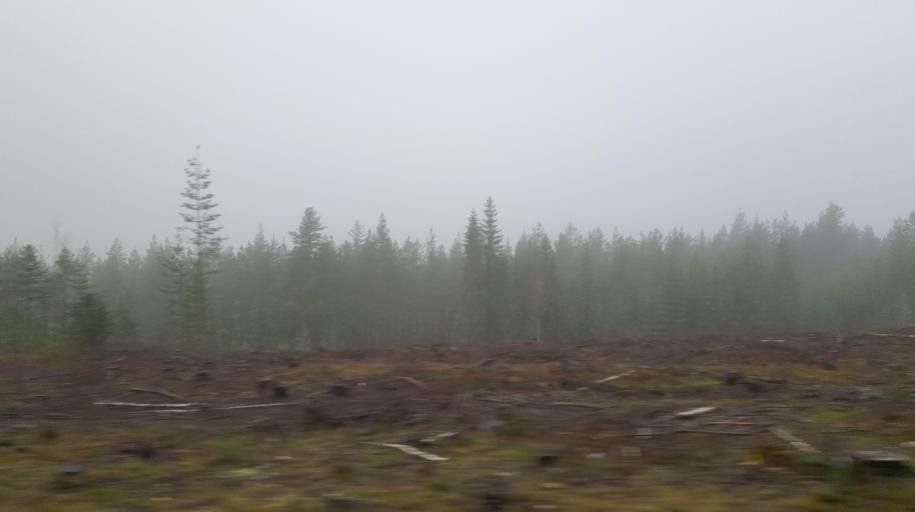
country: NO
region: Buskerud
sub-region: Sigdal
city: Prestfoss
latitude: 60.1028
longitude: 9.8114
